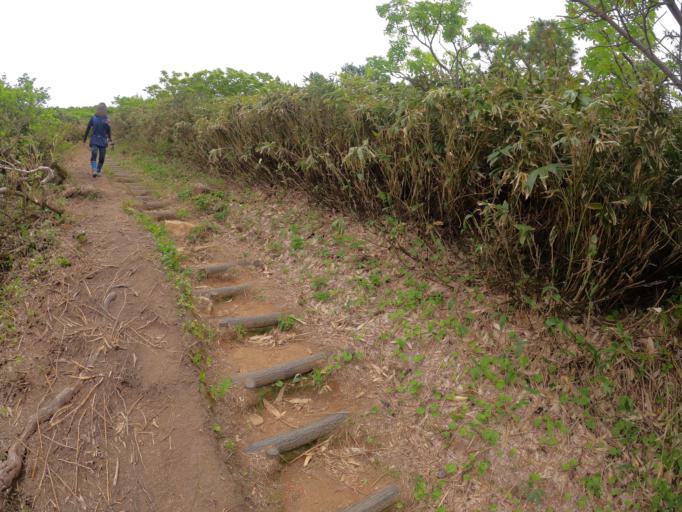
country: JP
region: Iwate
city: Ichinoseki
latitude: 38.9664
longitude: 140.7923
